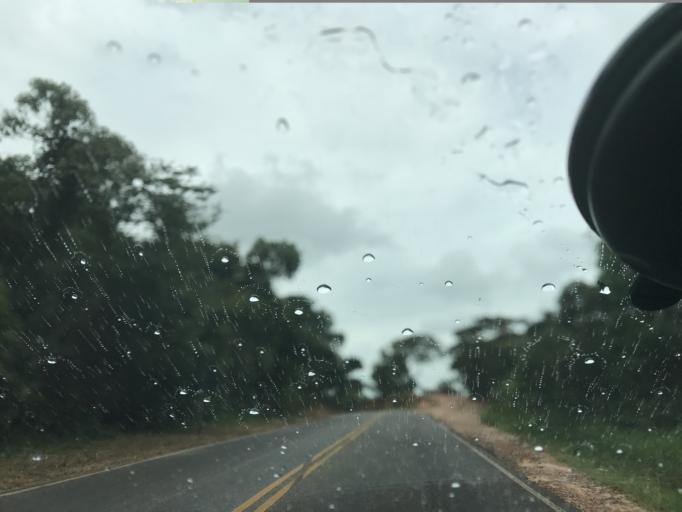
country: BR
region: Minas Gerais
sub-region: Conceicao Do Rio Verde
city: Conceicao do Rio Verde
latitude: -21.6771
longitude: -45.0189
